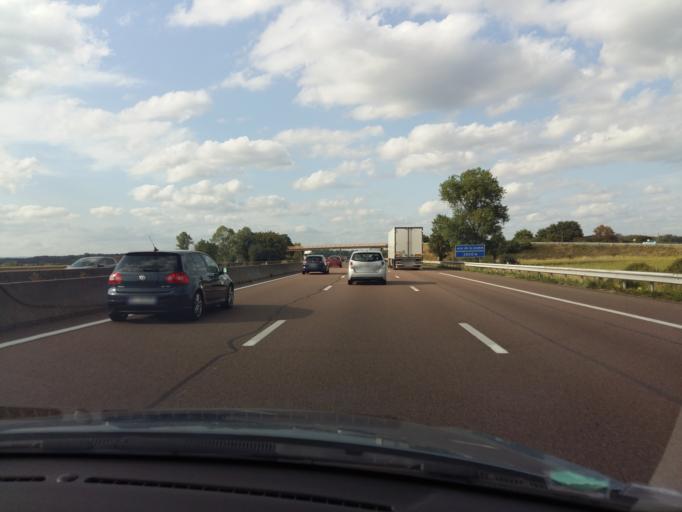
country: FR
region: Bourgogne
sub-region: Departement de Saone-et-Loire
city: Champforgeuil
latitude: 46.8388
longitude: 4.8320
